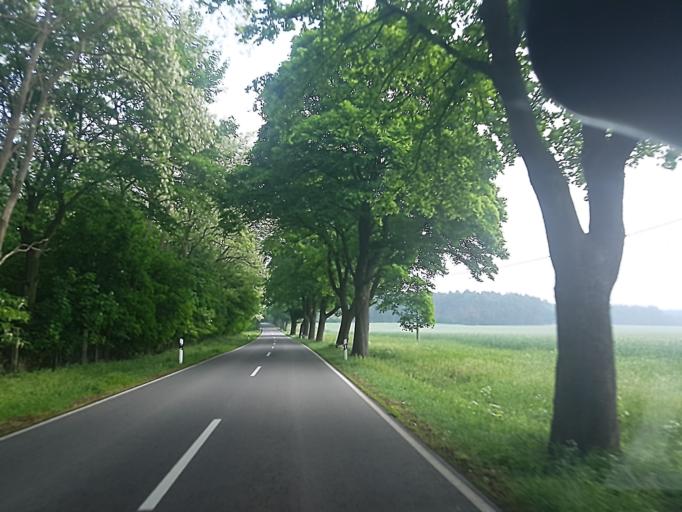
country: DE
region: Saxony-Anhalt
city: Klieken
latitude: 51.9910
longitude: 12.3596
